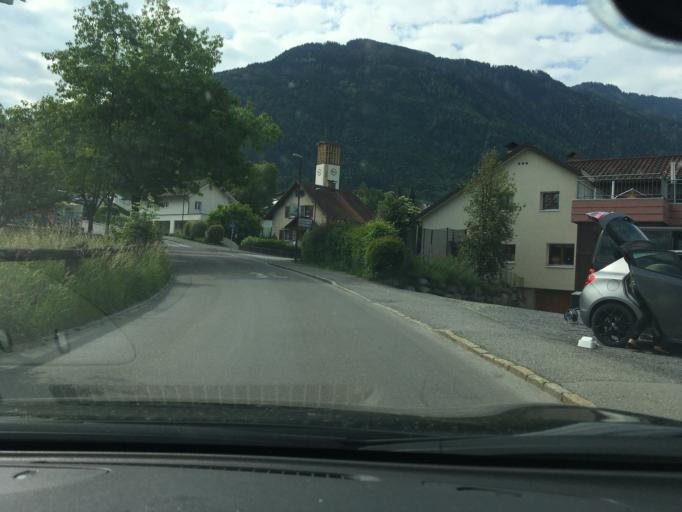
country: AT
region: Vorarlberg
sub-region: Politischer Bezirk Feldkirch
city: Feldkirch
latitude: 47.2277
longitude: 9.5804
